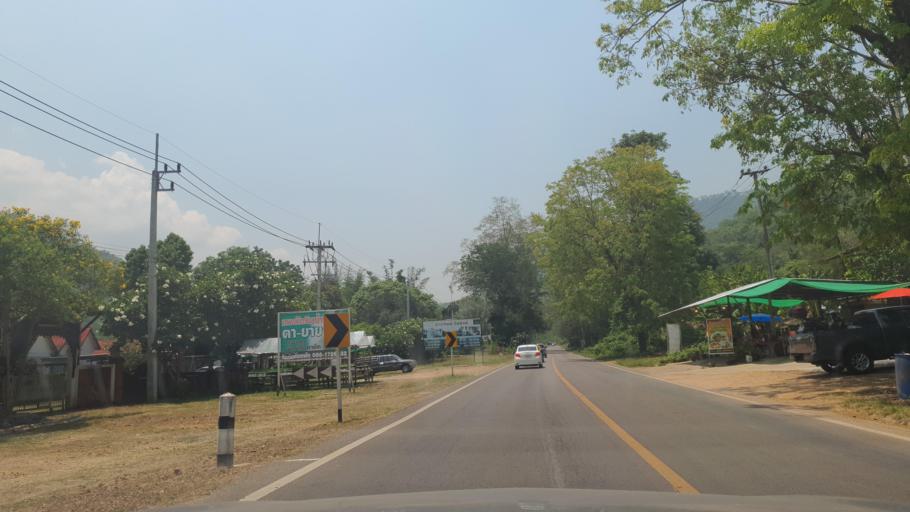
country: TH
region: Kanchanaburi
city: Sai Yok
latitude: 14.3515
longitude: 99.1758
